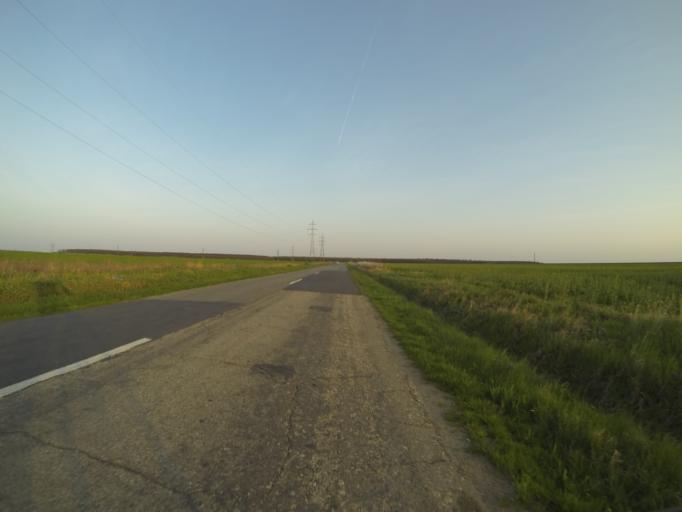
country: RO
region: Dolj
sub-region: Comuna Segarcea
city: Segarcea
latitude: 44.0730
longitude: 23.7949
